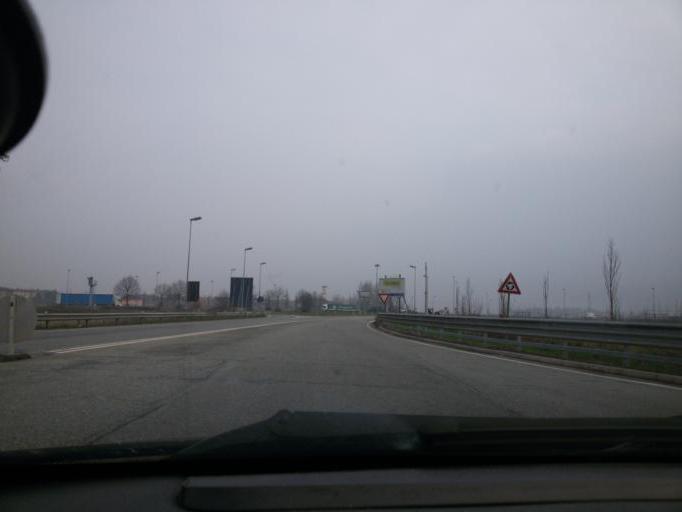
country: IT
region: Piedmont
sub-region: Provincia di Vercelli
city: Asigliano Vercellese
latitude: 45.2950
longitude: 8.3889
